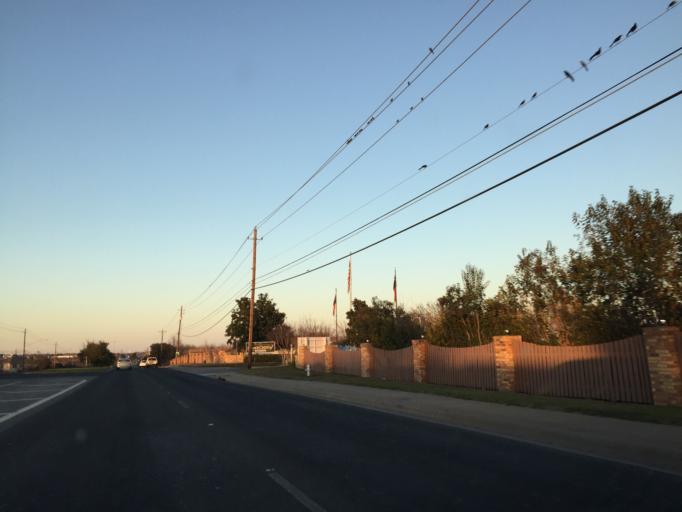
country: US
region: Texas
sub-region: Travis County
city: Pflugerville
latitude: 30.3918
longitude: -97.6460
